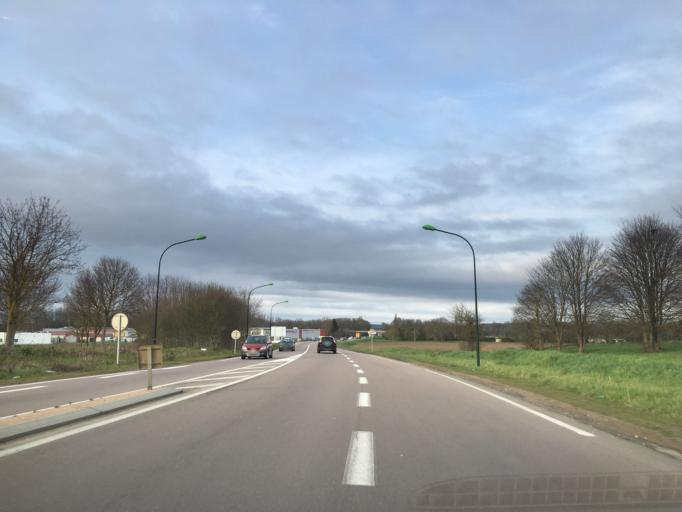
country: FR
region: Bourgogne
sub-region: Departement de l'Yonne
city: Maillot
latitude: 48.1752
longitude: 3.2948
